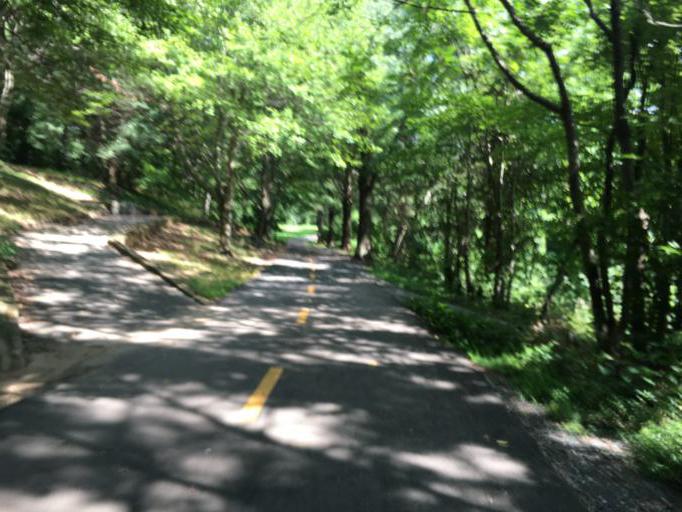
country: US
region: Virginia
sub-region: Fairfax County
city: Rose Hill
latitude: 38.8136
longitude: -77.1150
